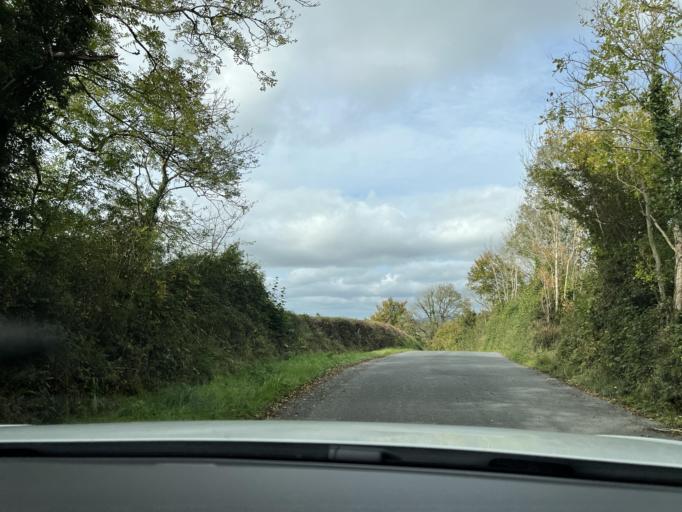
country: IE
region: Connaught
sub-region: County Leitrim
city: Carrick-on-Shannon
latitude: 53.9569
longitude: -8.0669
